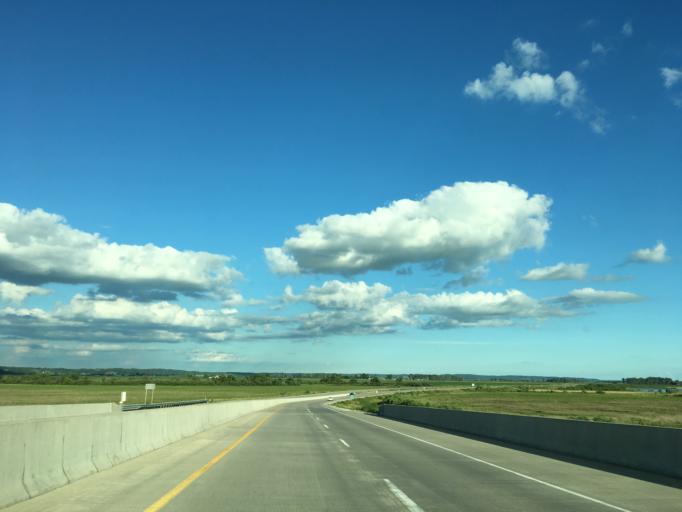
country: US
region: Nebraska
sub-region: Cass County
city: Plattsmouth
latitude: 41.0655
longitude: -95.8742
